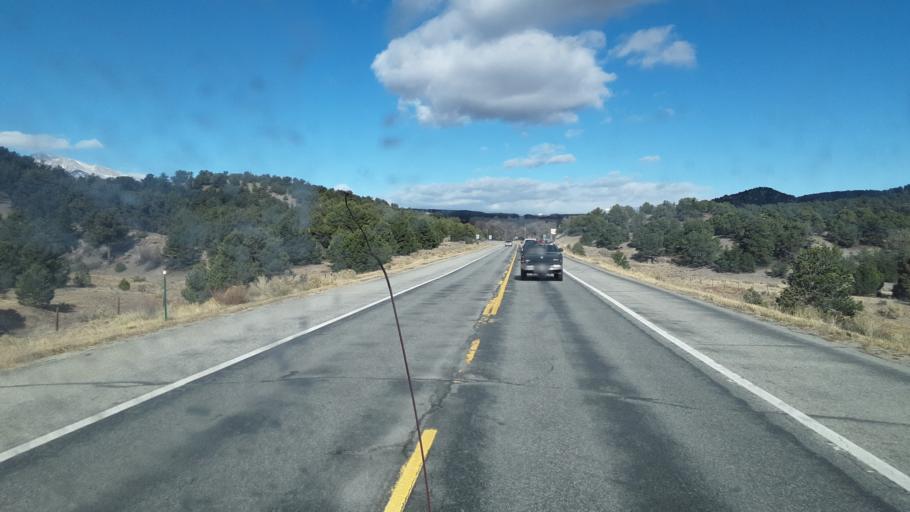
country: US
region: Colorado
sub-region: Chaffee County
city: Salida
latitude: 38.6308
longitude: -106.0788
